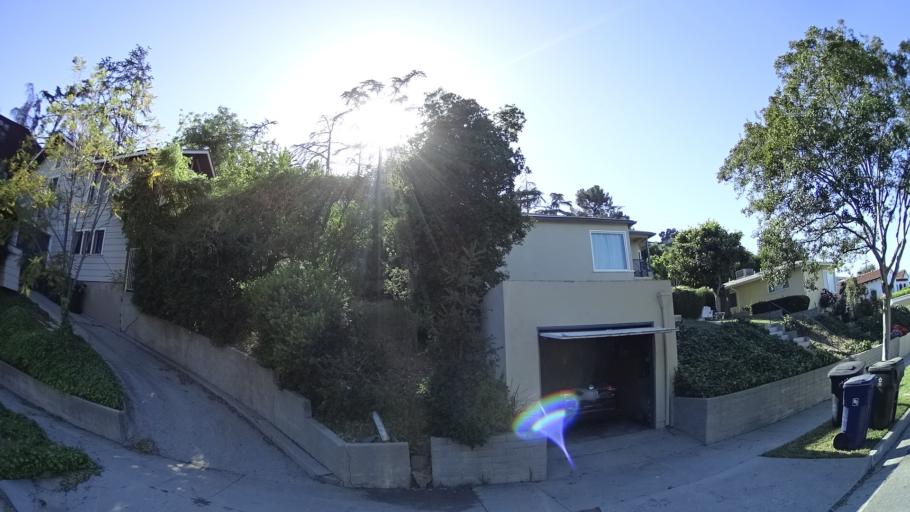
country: US
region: California
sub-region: Los Angeles County
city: Monterey Park
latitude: 34.0739
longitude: -118.1539
